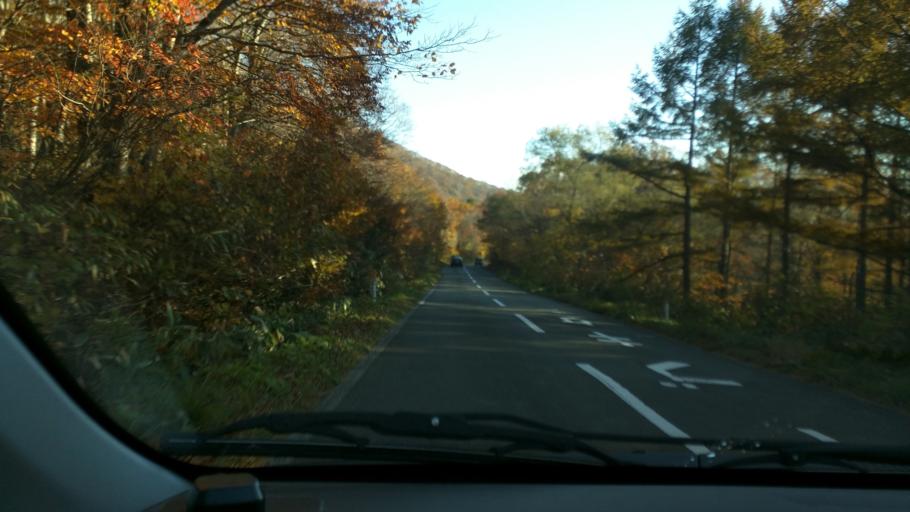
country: JP
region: Fukushima
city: Inawashiro
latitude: 37.6082
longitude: 140.0523
